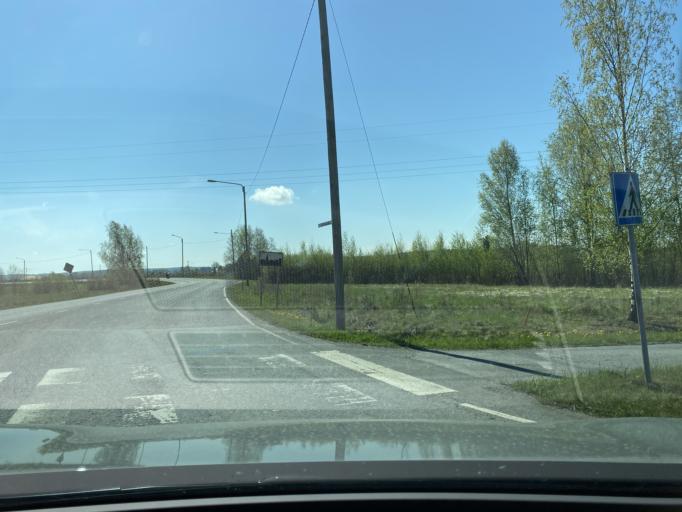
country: FI
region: Pirkanmaa
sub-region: Lounais-Pirkanmaa
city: Vammala
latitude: 61.3527
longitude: 22.8696
